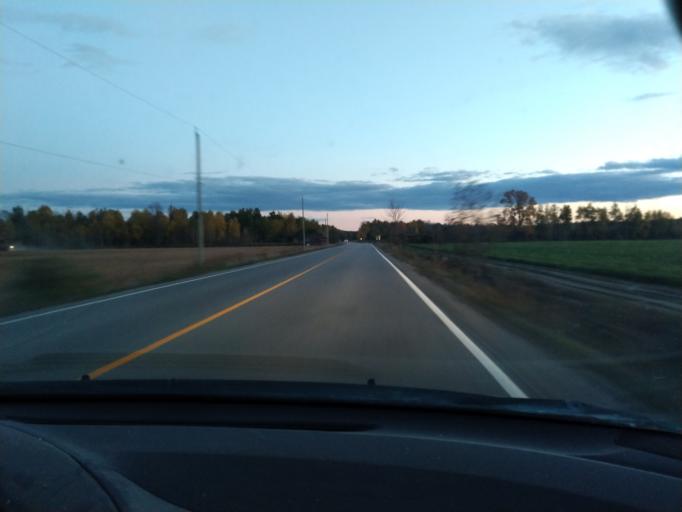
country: CA
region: Ontario
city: Bradford West Gwillimbury
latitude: 44.1920
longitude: -79.6628
